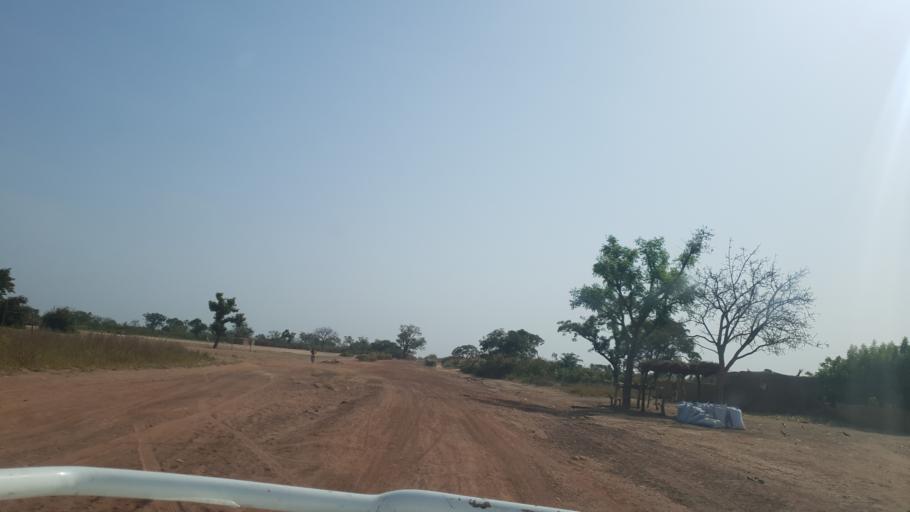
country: ML
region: Koulikoro
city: Dioila
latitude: 12.6692
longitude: -6.6709
